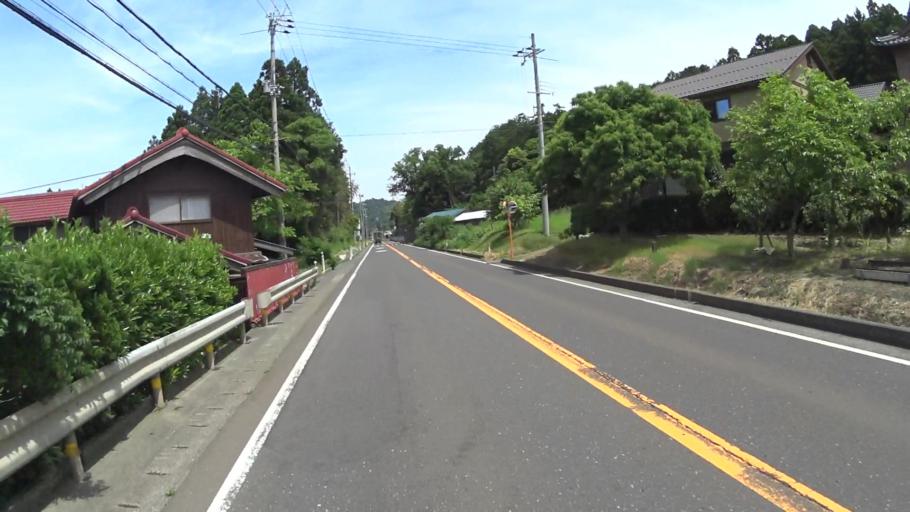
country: JP
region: Fukui
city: Obama
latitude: 35.4819
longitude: 135.6715
